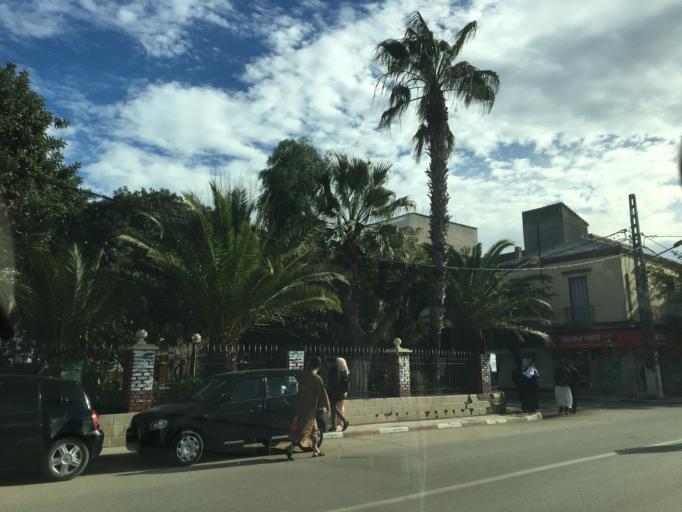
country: DZ
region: Alger
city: Ain Taya
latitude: 36.7906
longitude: 3.2499
